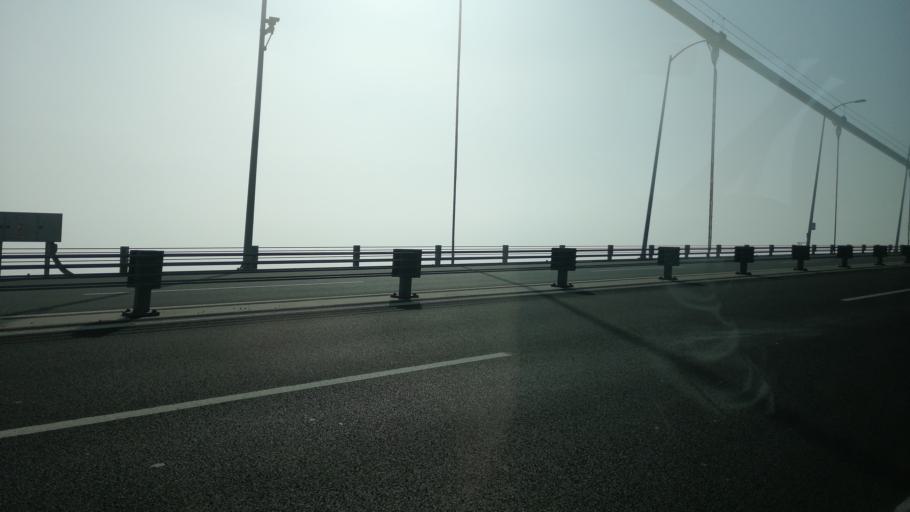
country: TR
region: Kocaeli
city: Tavsancil
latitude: 40.7570
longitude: 29.5160
